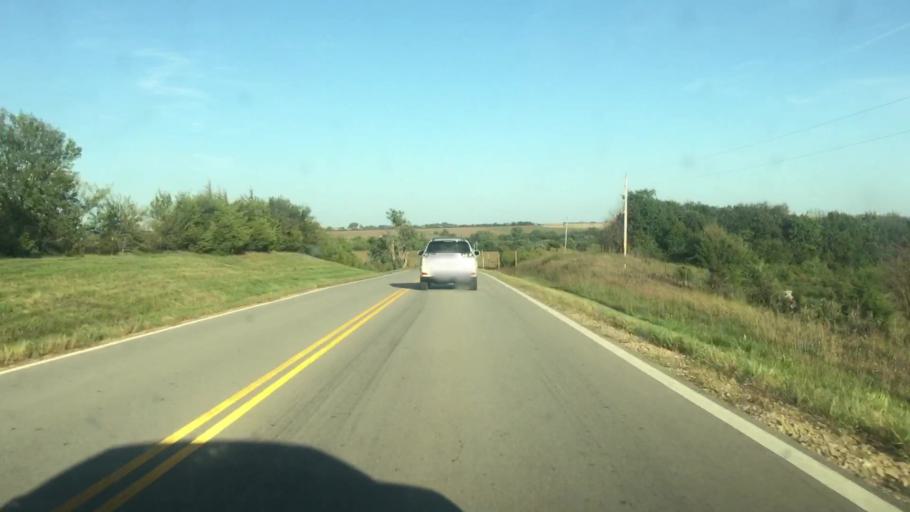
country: US
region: Kansas
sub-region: Brown County
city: Horton
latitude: 39.5874
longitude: -95.5445
